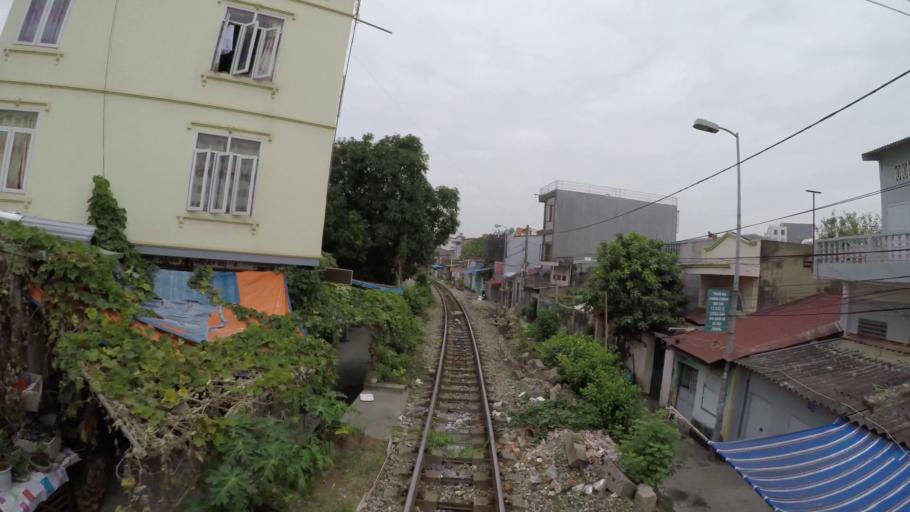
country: VN
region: Hai Phong
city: Haiphong
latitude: 20.8688
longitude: 106.6547
